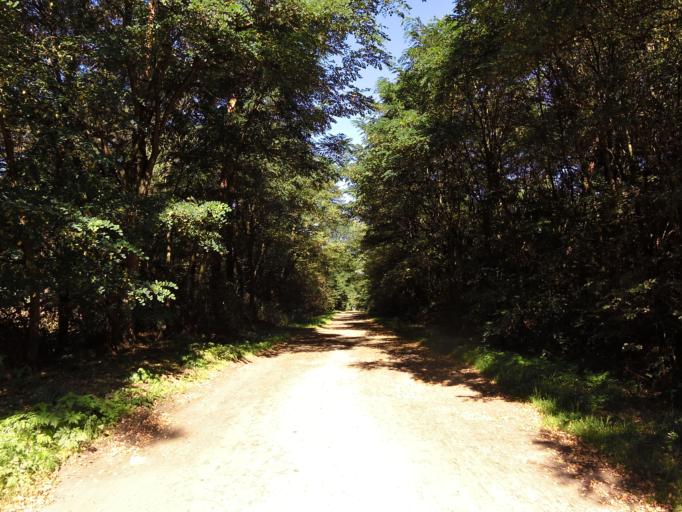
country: DE
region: Saxony
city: Strehla
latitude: 51.3861
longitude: 13.2567
